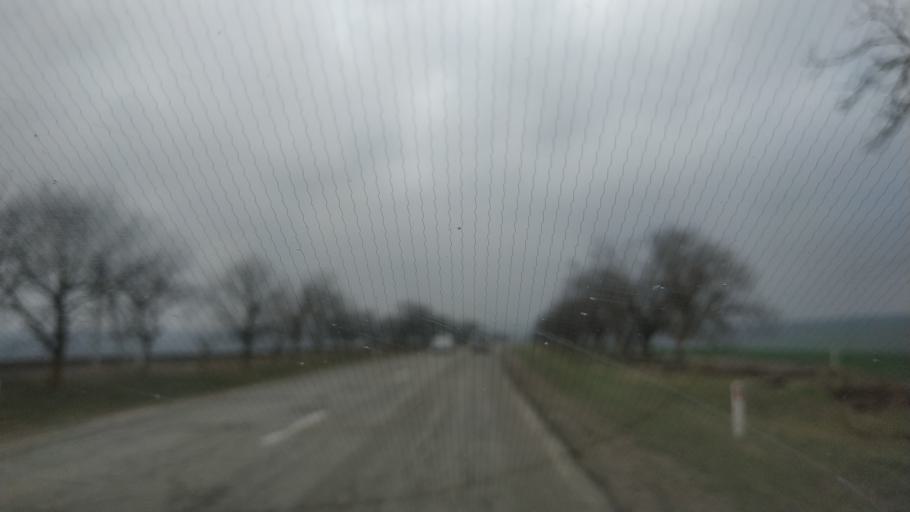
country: MD
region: Gagauzia
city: Comrat
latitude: 46.2566
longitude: 28.7532
